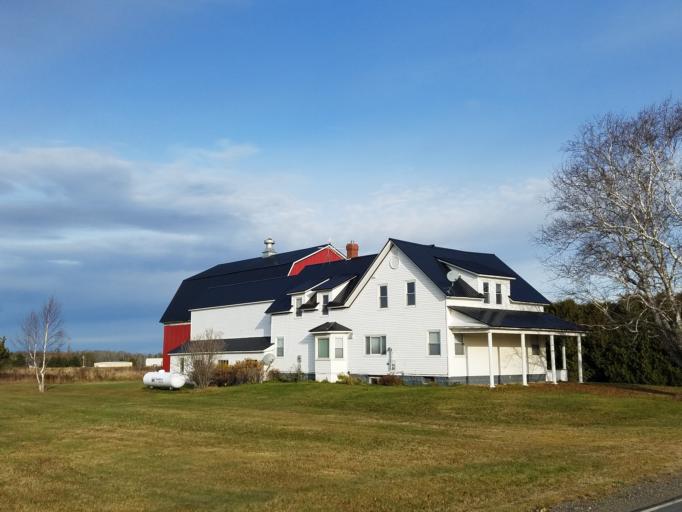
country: US
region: Maine
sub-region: Aroostook County
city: Presque Isle
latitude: 46.7334
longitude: -68.1779
